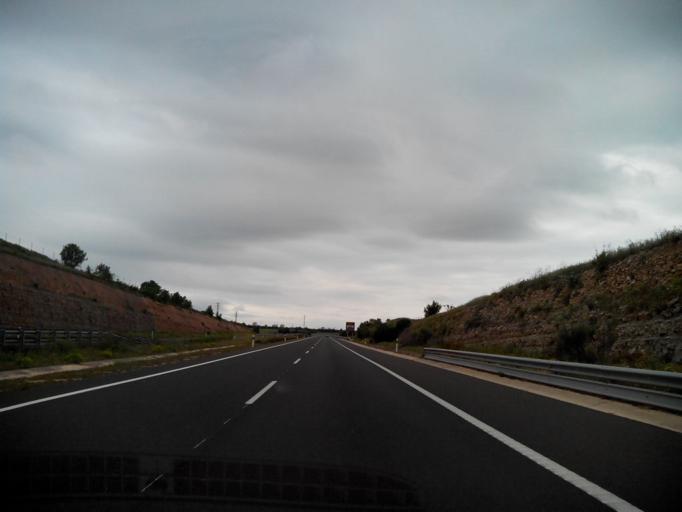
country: ES
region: Catalonia
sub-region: Provincia de Lleida
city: Cervera
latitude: 41.6897
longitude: 1.3090
